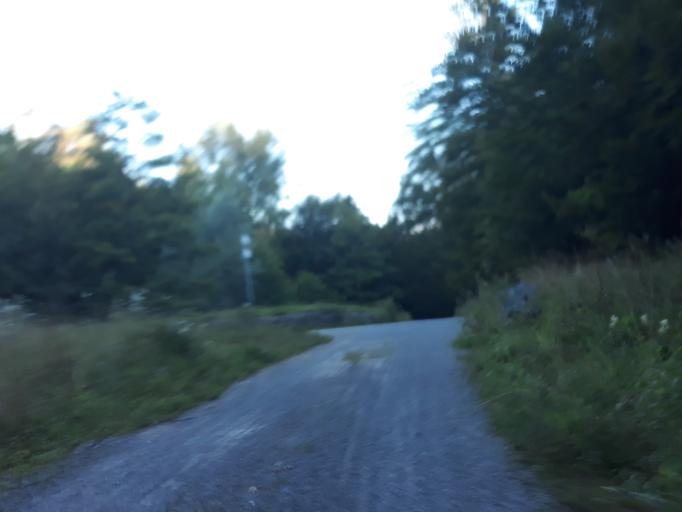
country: DE
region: Baden-Wuerttemberg
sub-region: Regierungsbezirk Stuttgart
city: Schonaich
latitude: 48.6717
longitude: 9.0395
